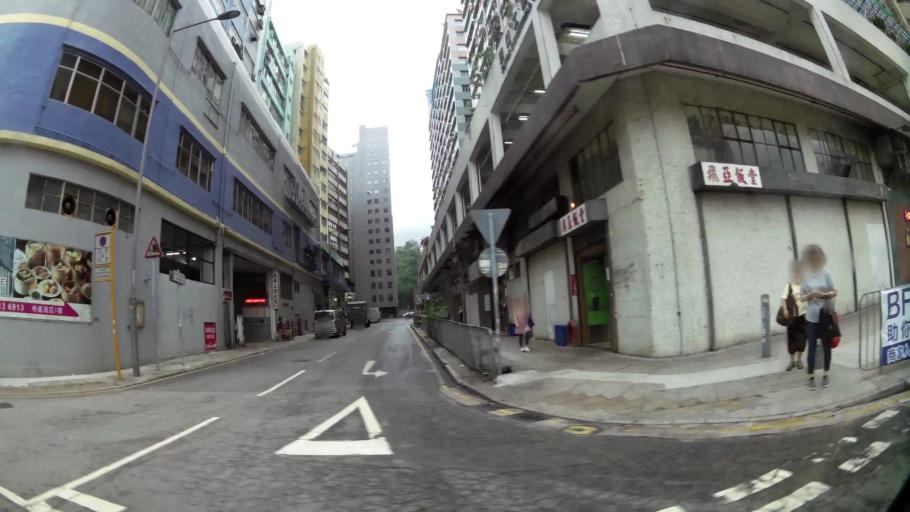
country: HK
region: Tsuen Wan
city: Tsuen Wan
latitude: 22.3693
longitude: 114.1303
